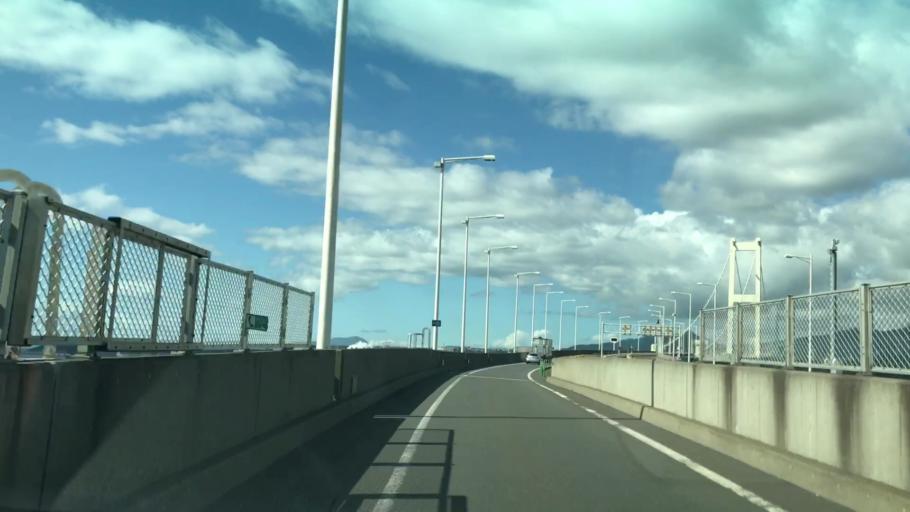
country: JP
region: Hokkaido
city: Muroran
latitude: 42.3434
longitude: 140.9493
